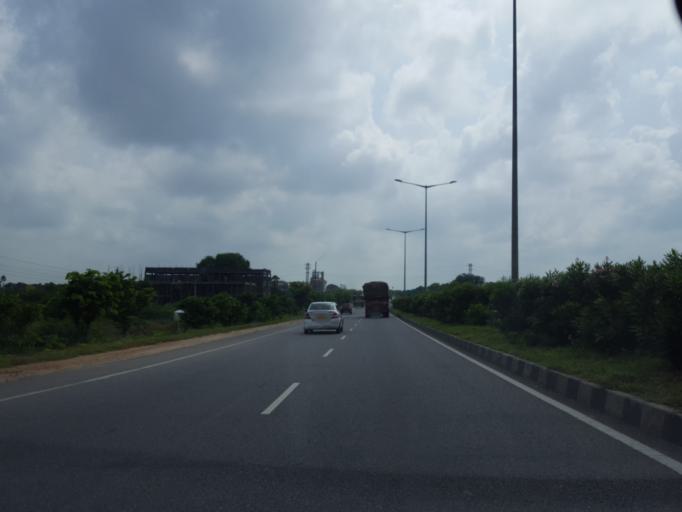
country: IN
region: Telangana
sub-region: Nalgonda
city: Bhongir
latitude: 17.2319
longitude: 78.9884
